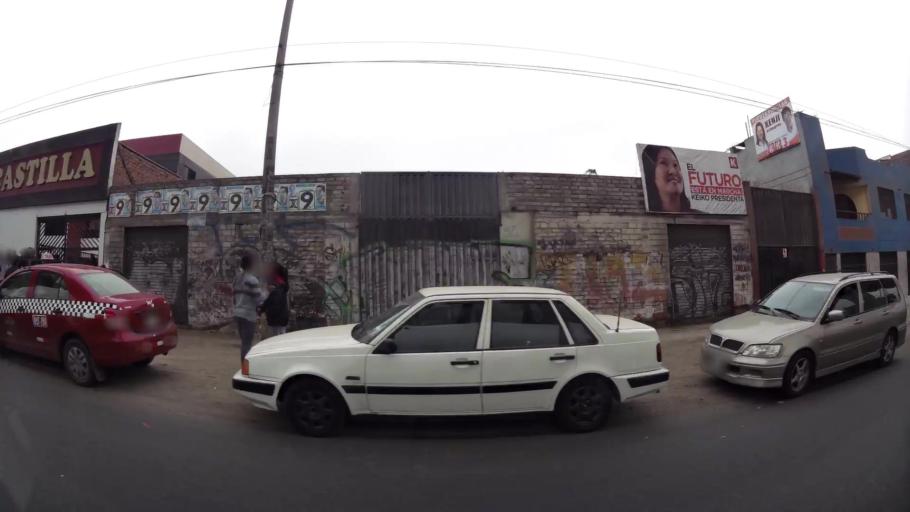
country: PE
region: Lima
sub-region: Lima
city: Independencia
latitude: -11.9709
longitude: -76.9953
